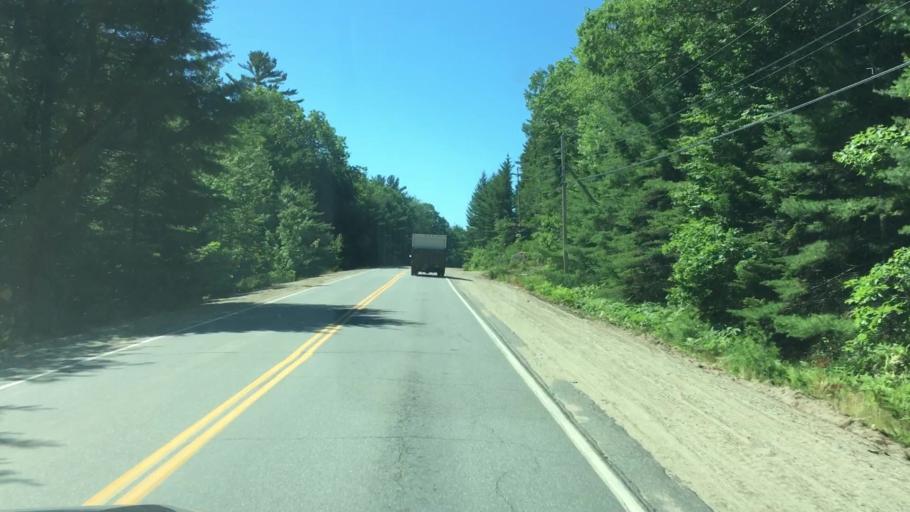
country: US
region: Maine
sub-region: Hancock County
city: Sedgwick
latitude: 44.3754
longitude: -68.5680
